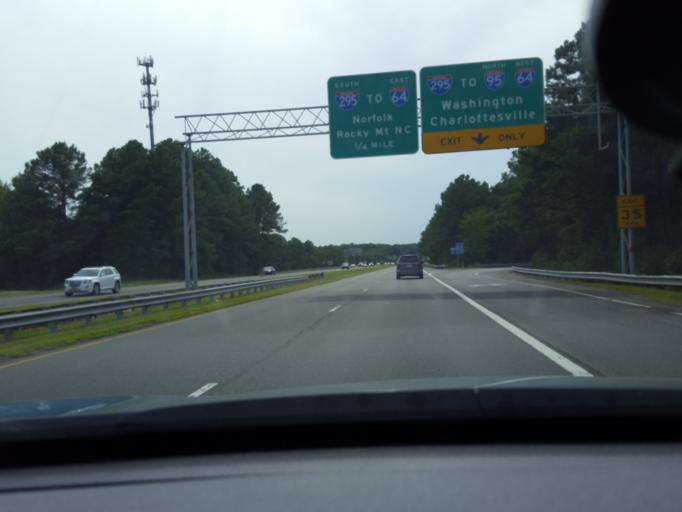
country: US
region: Virginia
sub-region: Henrico County
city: Chamberlayne
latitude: 37.6468
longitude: -77.4094
